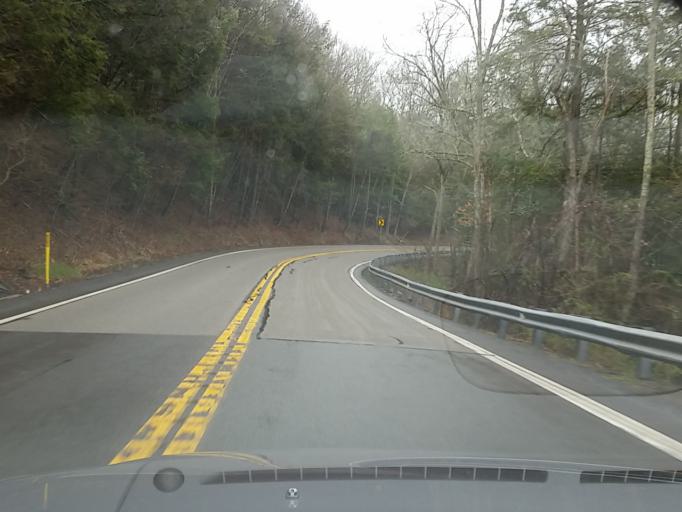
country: US
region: Pennsylvania
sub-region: Luzerne County
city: Nanticoke
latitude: 41.2522
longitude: -76.0037
